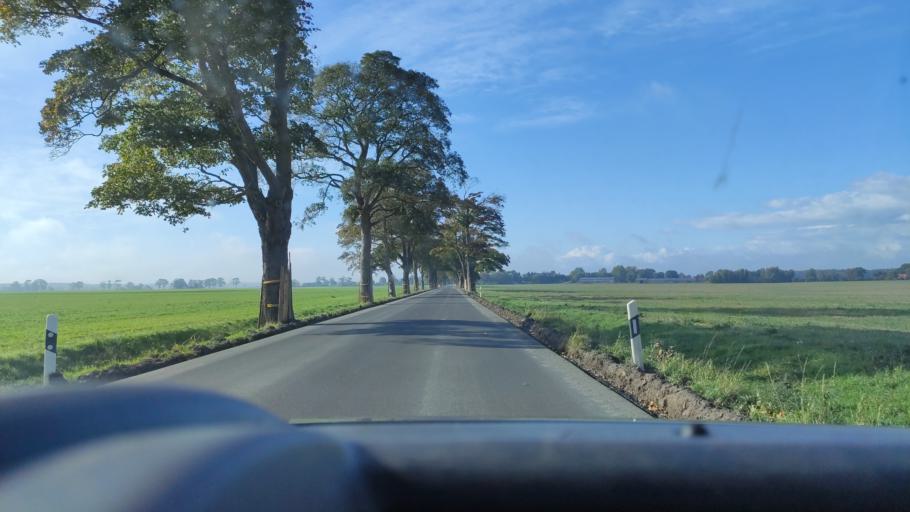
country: DE
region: Mecklenburg-Vorpommern
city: Grimmen
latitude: 54.0556
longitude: 13.1362
